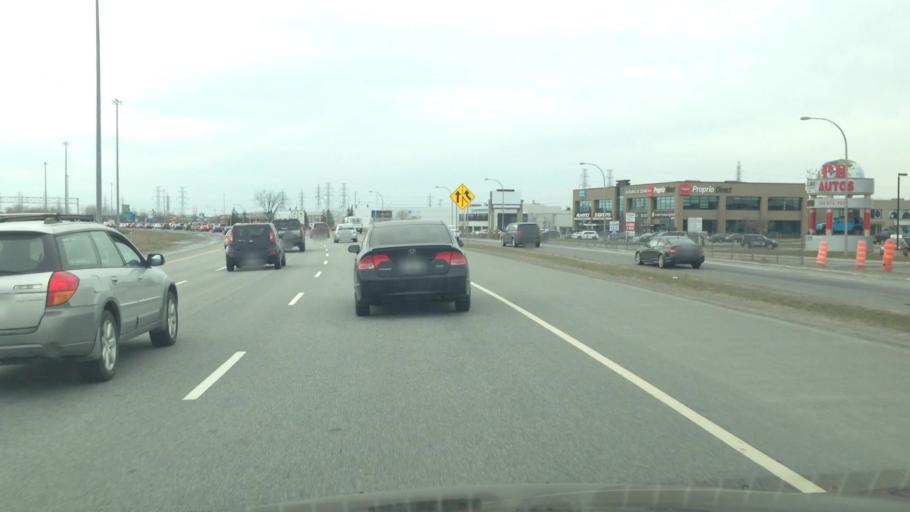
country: CA
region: Quebec
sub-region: Laurentides
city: Rosemere
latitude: 45.5814
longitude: -73.7605
